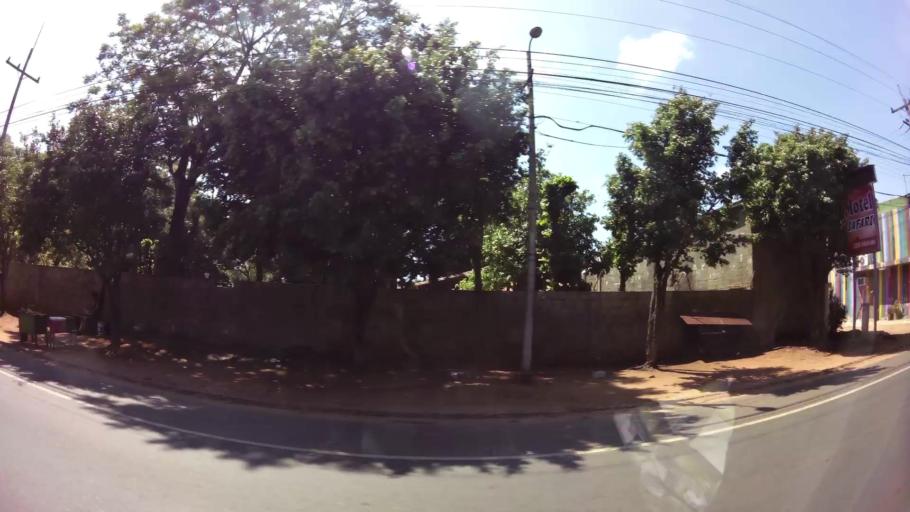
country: PY
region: Central
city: San Lorenzo
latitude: -25.3136
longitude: -57.5068
